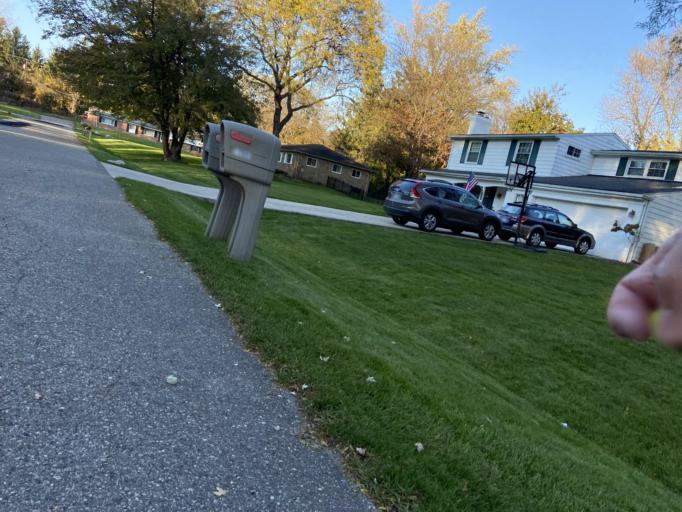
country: US
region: Michigan
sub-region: Oakland County
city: Franklin
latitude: 42.5349
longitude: -83.3352
